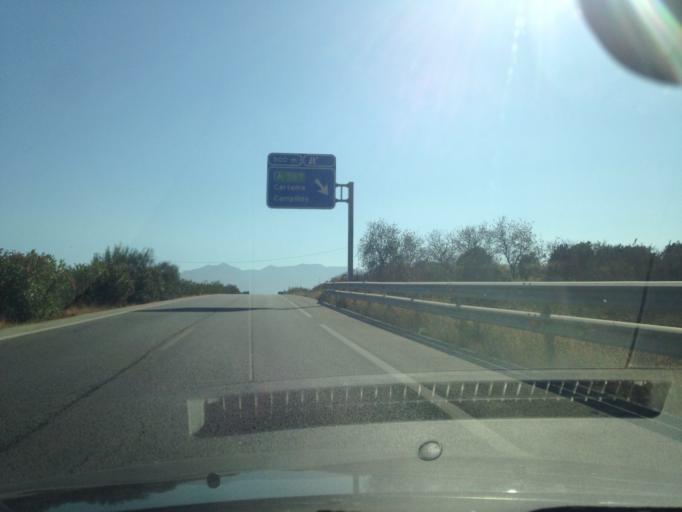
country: ES
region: Andalusia
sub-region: Provincia de Malaga
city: Alhaurin de la Torre
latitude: 36.7237
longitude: -4.5534
